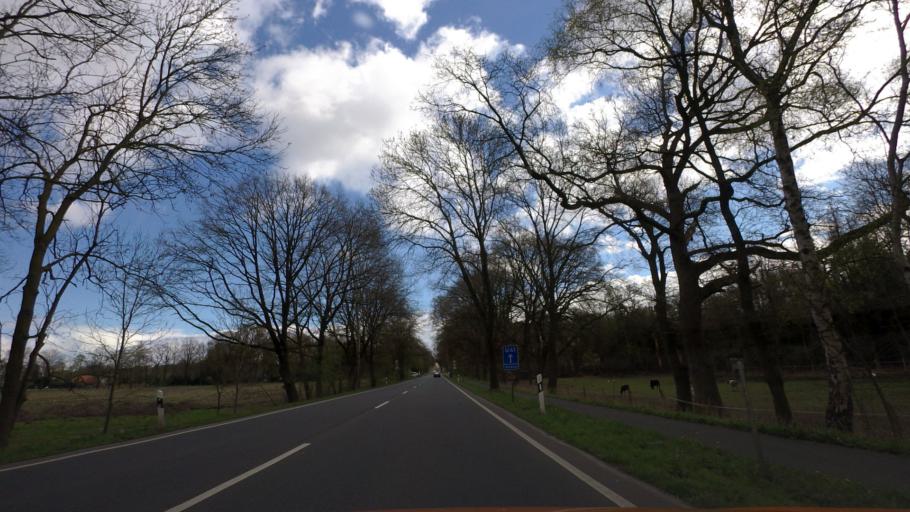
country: DE
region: Lower Saxony
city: Botersen
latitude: 53.1208
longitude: 9.3174
